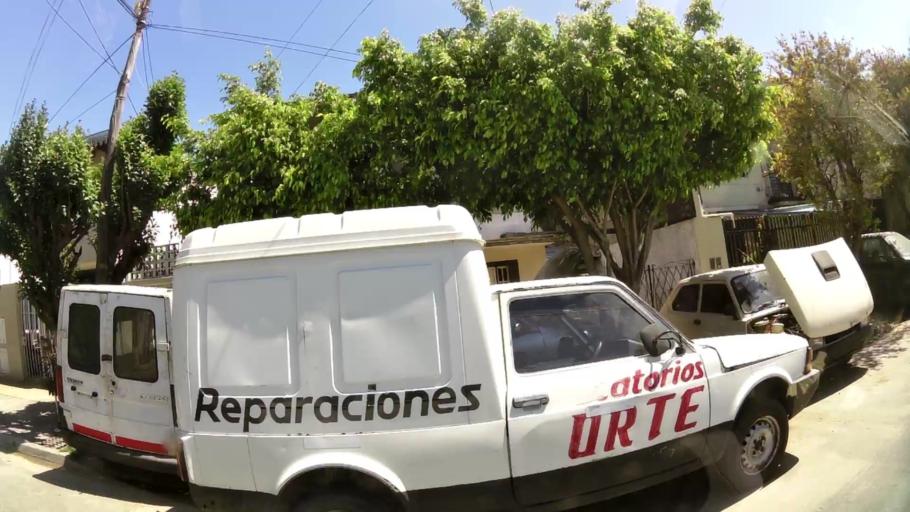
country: AR
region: Buenos Aires
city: Caseros
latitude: -34.5711
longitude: -58.5704
